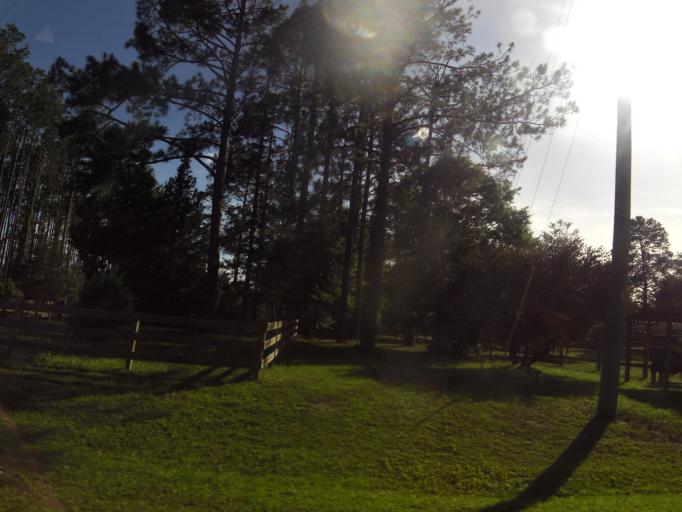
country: US
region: Florida
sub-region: Nassau County
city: Nassau Village-Ratliff
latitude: 30.4744
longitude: -81.8418
